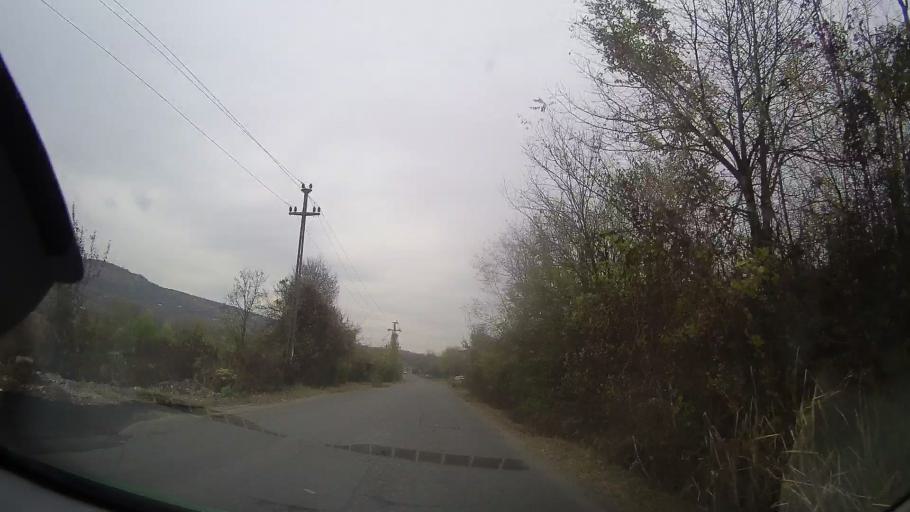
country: RO
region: Prahova
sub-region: Oras Urlati
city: Urlati
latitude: 45.0079
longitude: 26.2282
